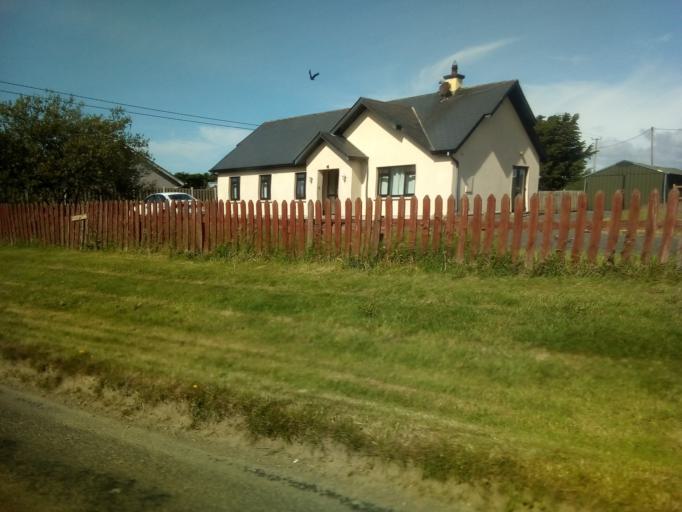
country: IE
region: Leinster
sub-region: Loch Garman
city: Loch Garman
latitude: 52.2119
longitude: -6.5415
